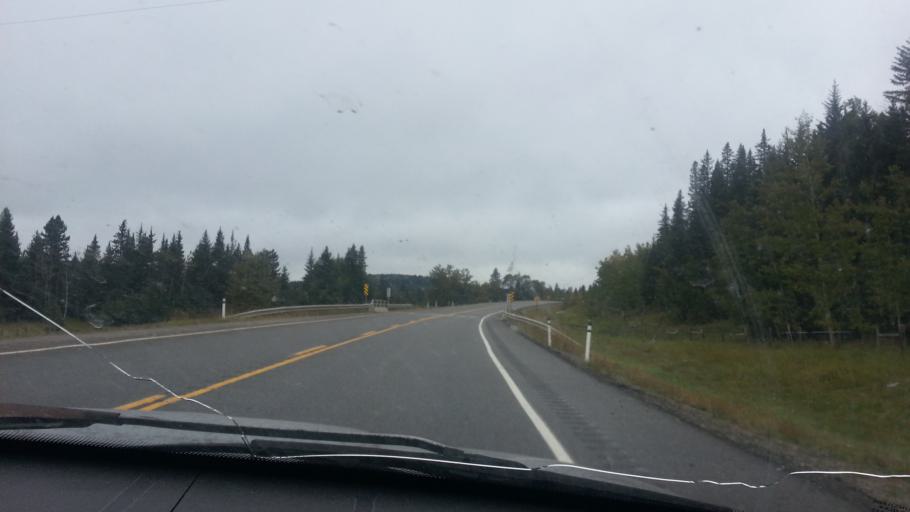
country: CA
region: Alberta
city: Cochrane
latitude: 51.0371
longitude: -114.7187
